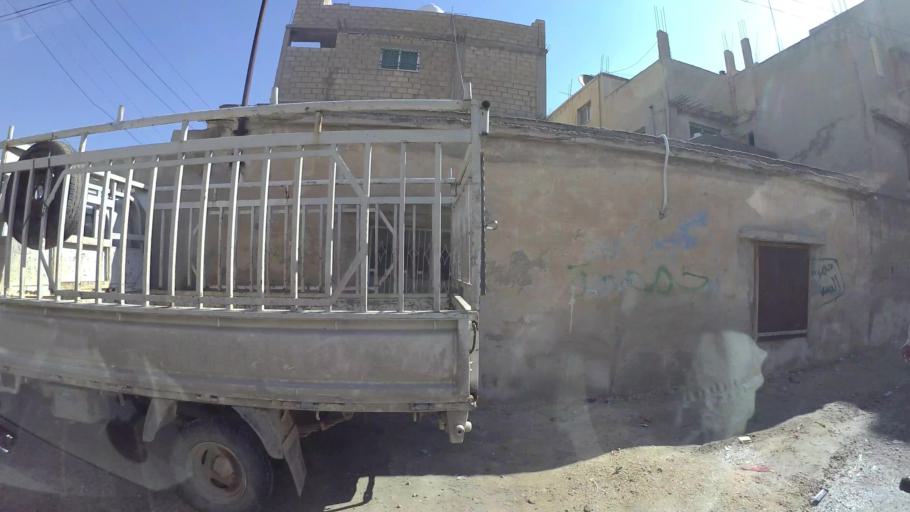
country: JO
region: Amman
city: Amman
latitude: 31.9887
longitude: 35.9856
